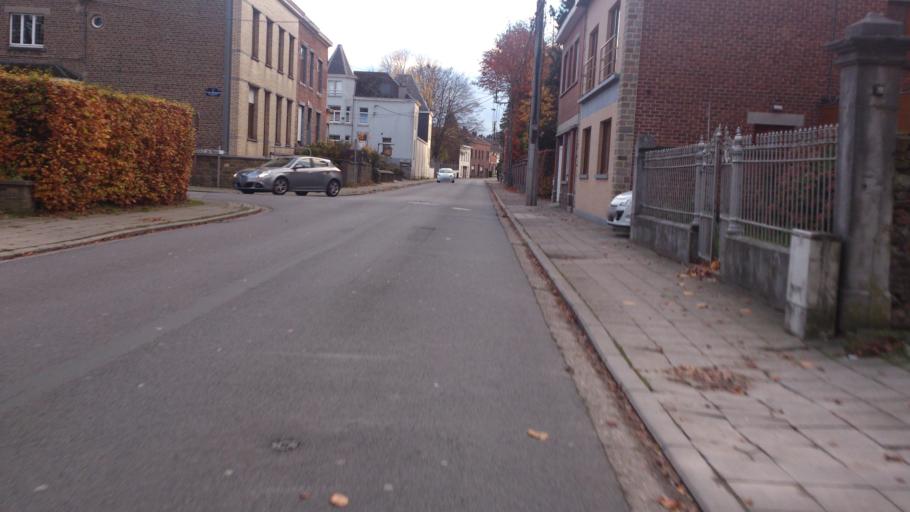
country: BE
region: Wallonia
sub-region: Province de Liege
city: Fleron
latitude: 50.6183
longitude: 5.6824
